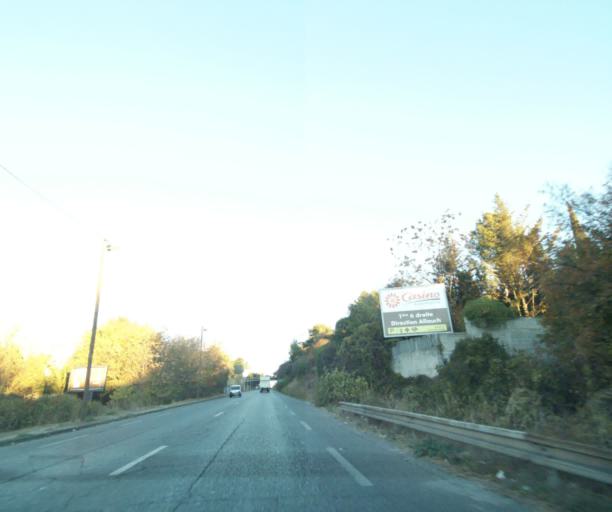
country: FR
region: Provence-Alpes-Cote d'Azur
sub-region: Departement des Bouches-du-Rhone
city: Allauch
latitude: 43.3099
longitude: 5.4662
